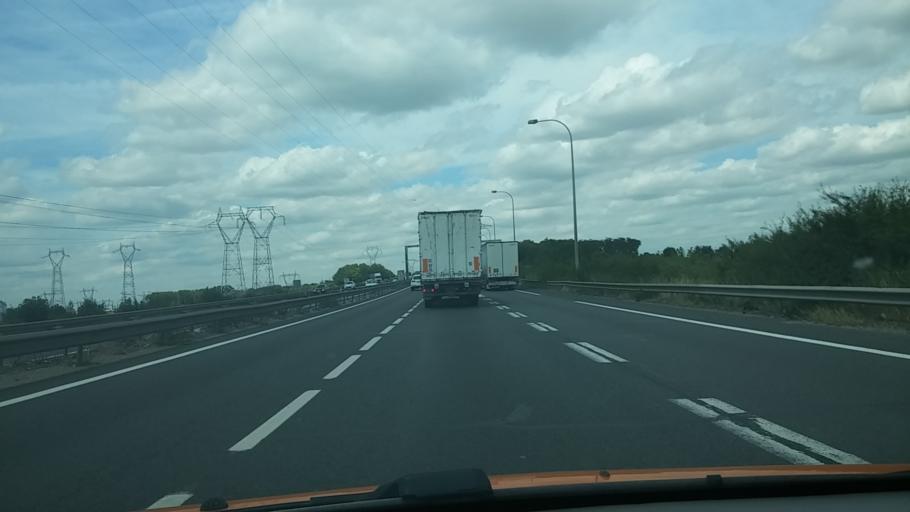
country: FR
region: Ile-de-France
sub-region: Departement de Seine-et-Marne
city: Mitry-Mory
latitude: 48.9741
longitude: 2.5886
